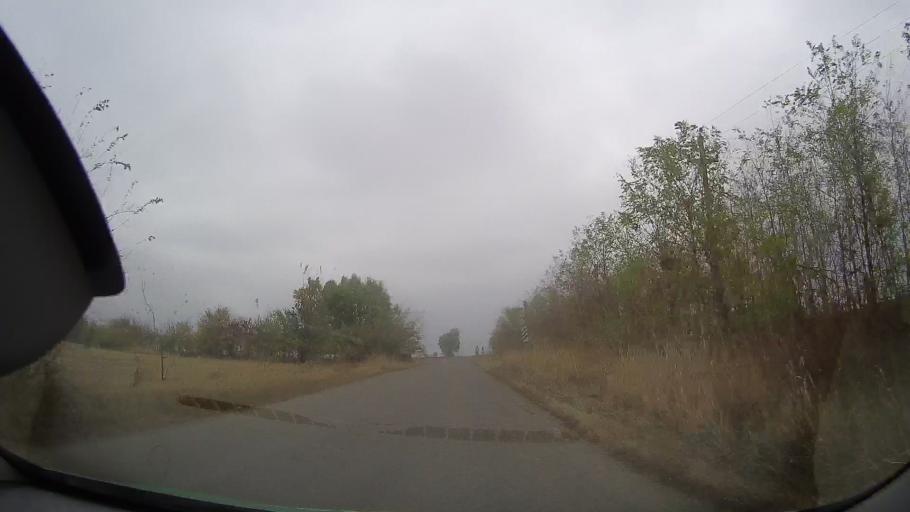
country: RO
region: Buzau
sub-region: Comuna Glodeanu-Silistea
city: Glodeanu-Silistea
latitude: 44.8112
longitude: 26.8540
